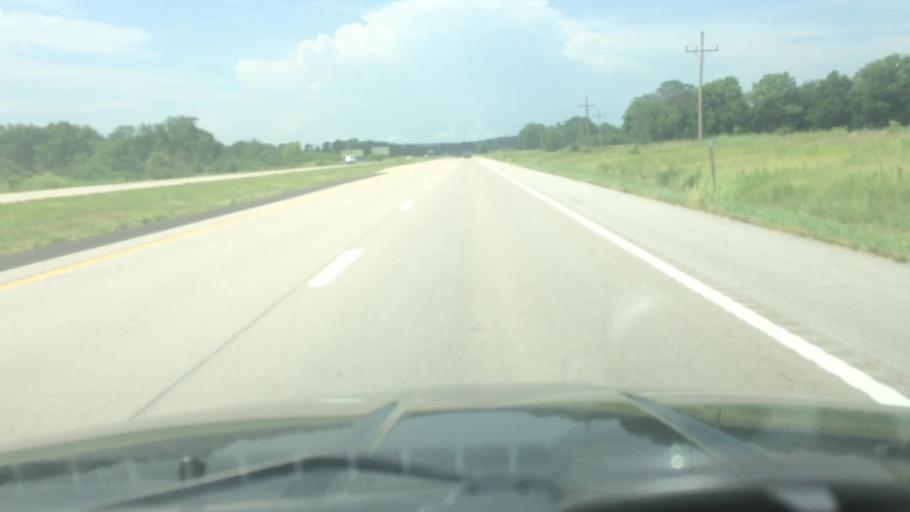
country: US
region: Missouri
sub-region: Polk County
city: Humansville
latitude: 37.8120
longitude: -93.6060
